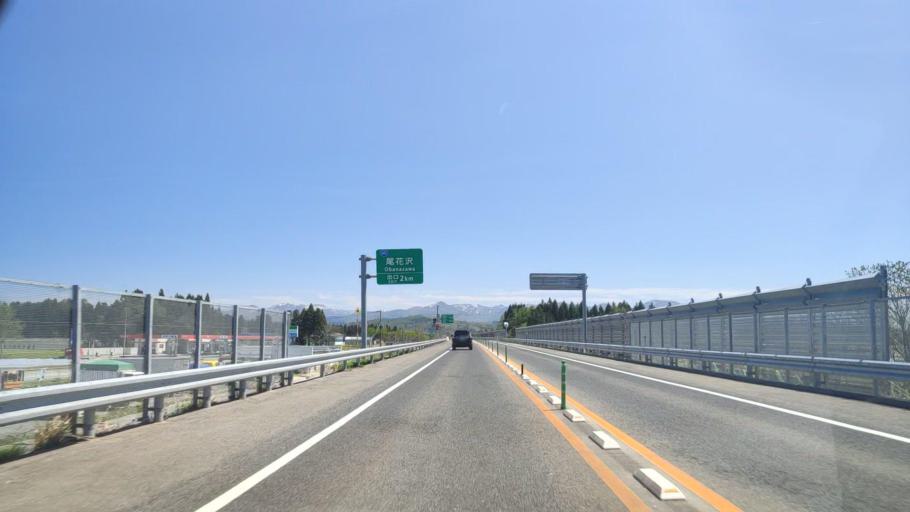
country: JP
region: Yamagata
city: Obanazawa
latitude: 38.6229
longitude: 140.3796
